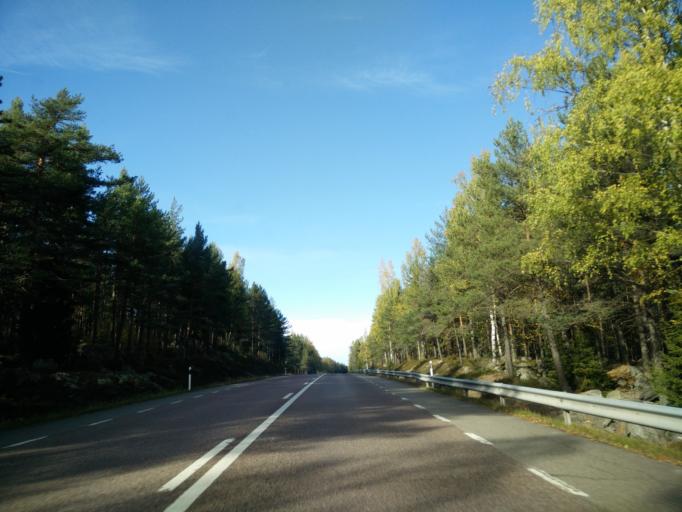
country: SE
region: Gaevleborg
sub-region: Hudiksvalls Kommun
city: Iggesund
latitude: 61.5819
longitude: 17.0262
